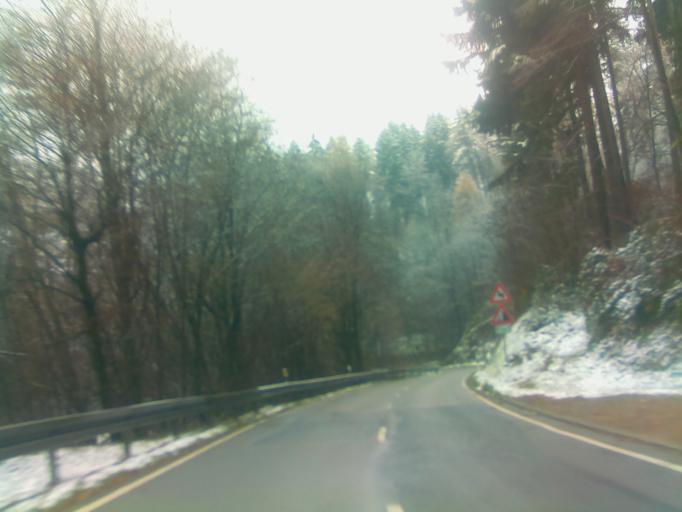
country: DE
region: Hesse
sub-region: Regierungsbezirk Darmstadt
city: Birkenau
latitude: 49.5222
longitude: 8.7338
